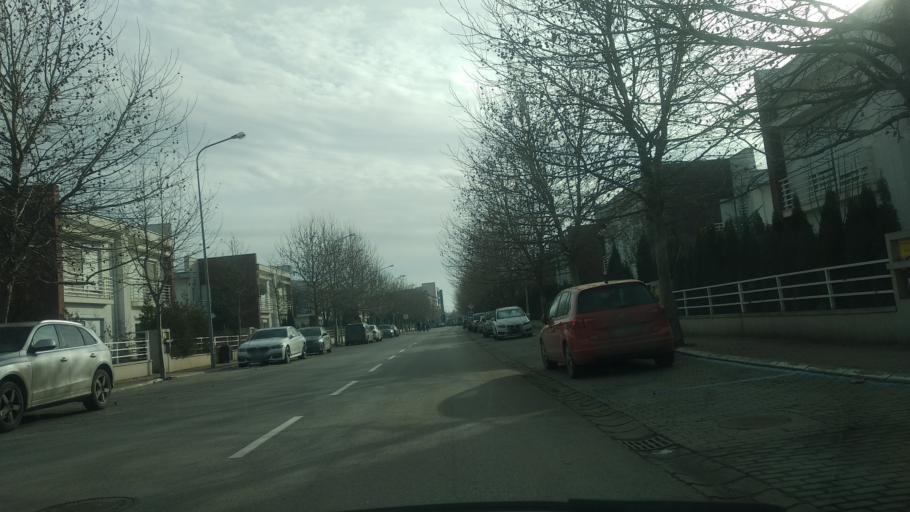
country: XK
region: Pristina
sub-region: Komuna e Gracanices
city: Glanica
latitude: 42.5879
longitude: 21.1079
